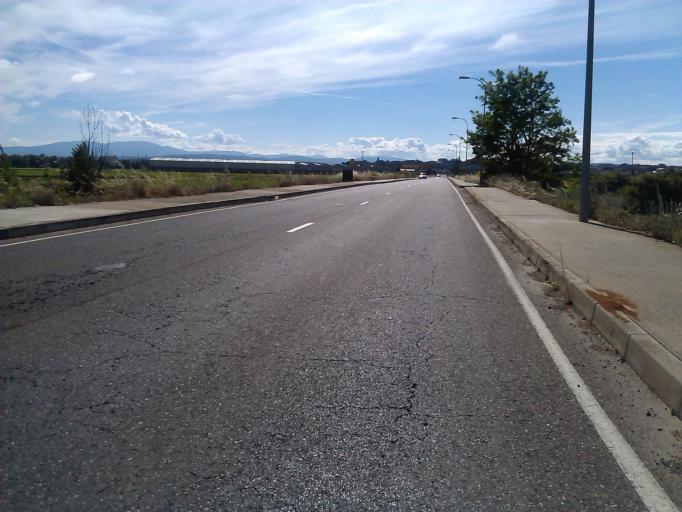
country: ES
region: Castille and Leon
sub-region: Provincia de Leon
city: San Justo de la Vega
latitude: 42.4541
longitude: -6.0280
